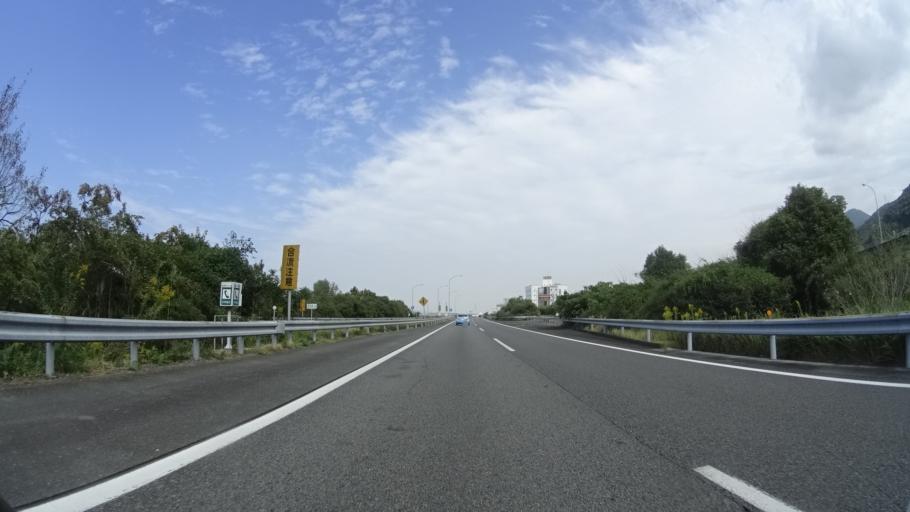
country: JP
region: Kumamoto
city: Yatsushiro
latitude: 32.5035
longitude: 130.6461
